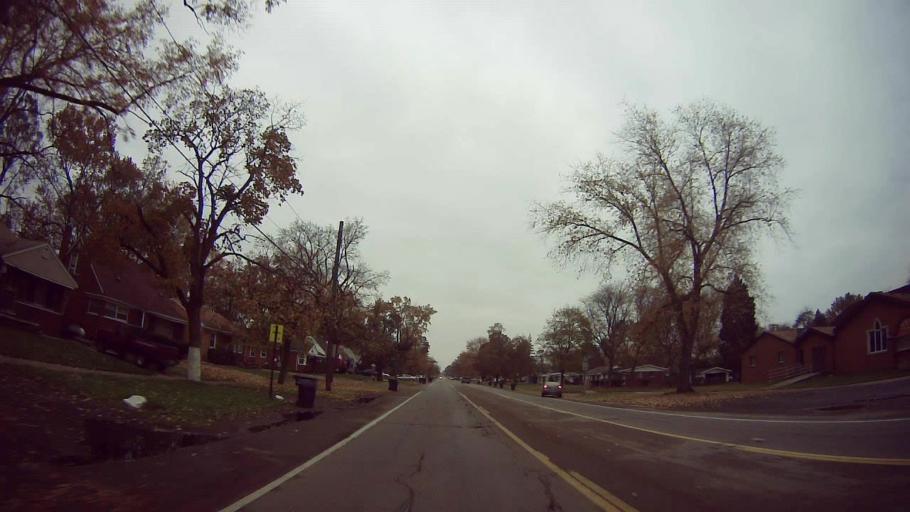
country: US
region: Michigan
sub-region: Oakland County
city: Southfield
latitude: 42.4402
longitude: -83.2587
